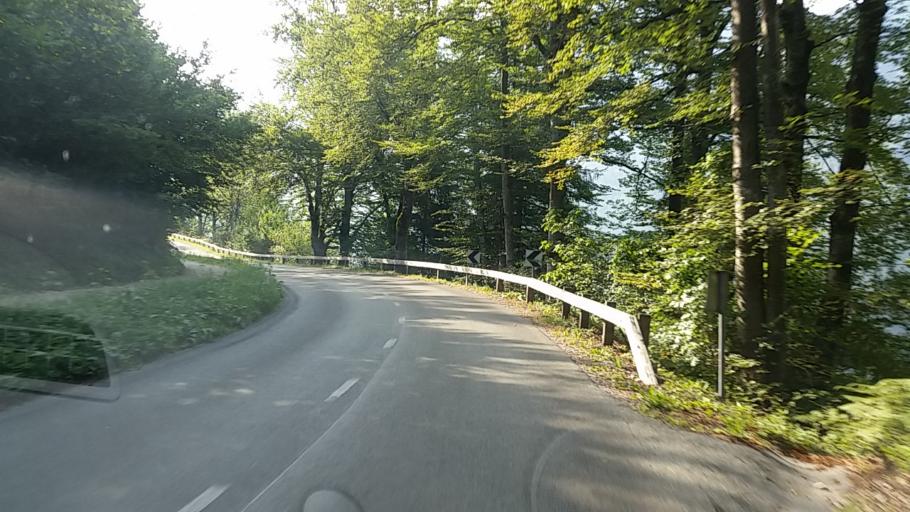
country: SI
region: Bohinj
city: Bohinjska Bistrica
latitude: 46.2774
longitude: 13.8806
